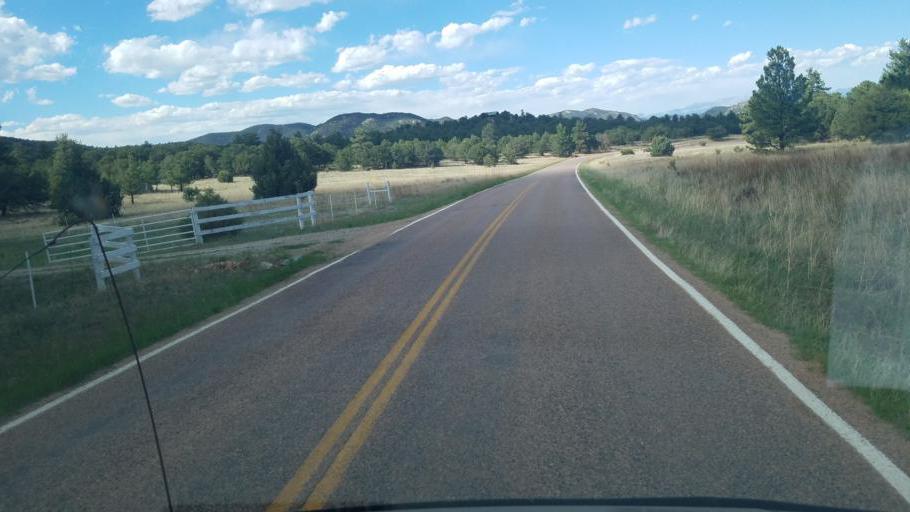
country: US
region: Colorado
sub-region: Custer County
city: Westcliffe
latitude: 38.3424
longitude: -105.4850
